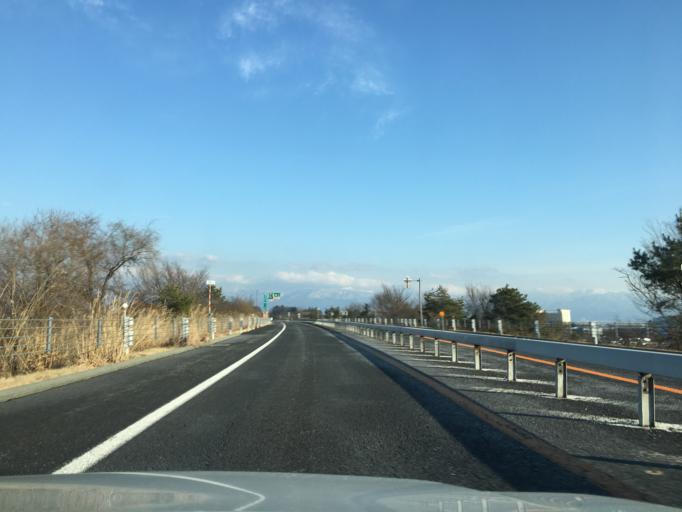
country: JP
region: Yamagata
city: Sagae
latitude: 38.3691
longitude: 140.2512
